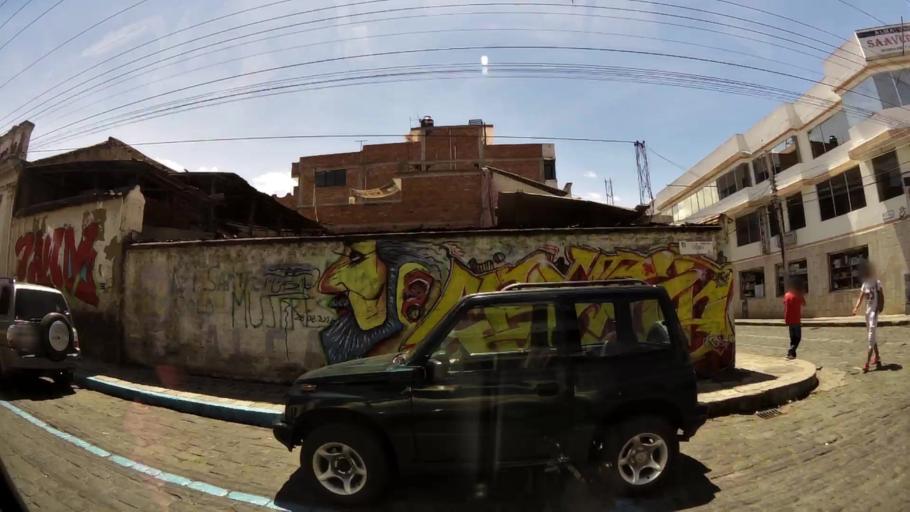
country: EC
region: Chimborazo
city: Riobamba
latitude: -1.6749
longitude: -78.6486
